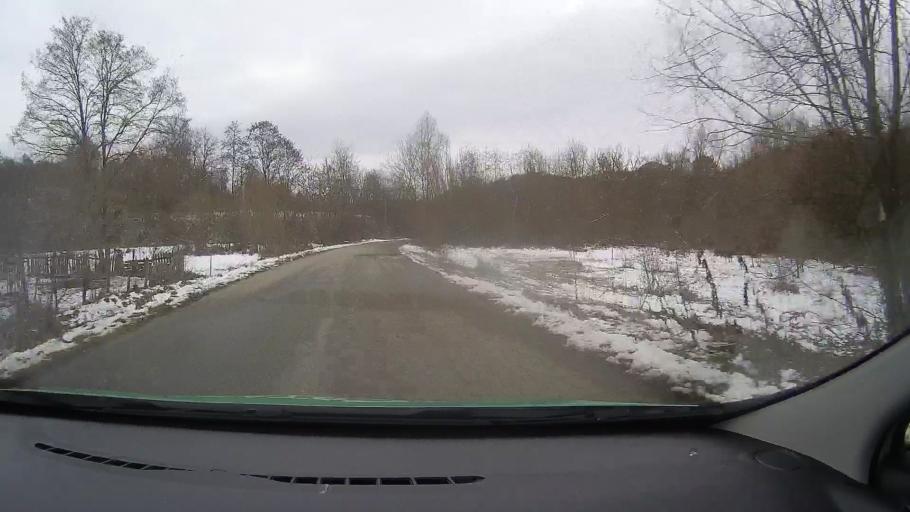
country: RO
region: Hunedoara
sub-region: Comuna Balsa
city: Balsa
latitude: 46.0403
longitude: 23.0738
